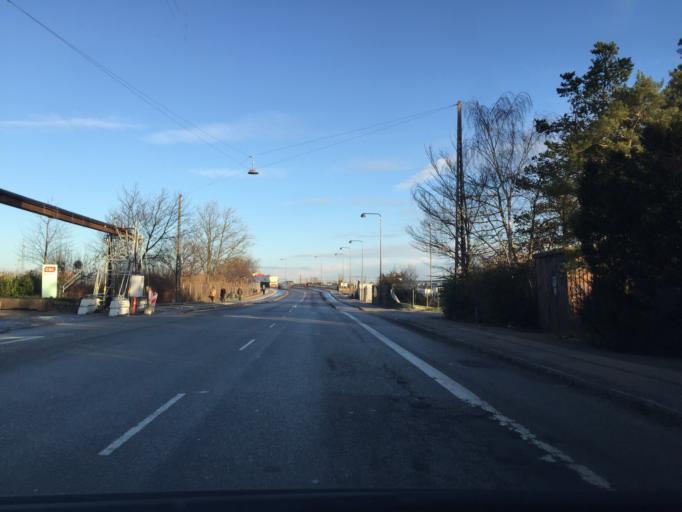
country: DK
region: Capital Region
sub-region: Hvidovre Kommune
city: Hvidovre
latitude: 55.6568
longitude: 12.5005
